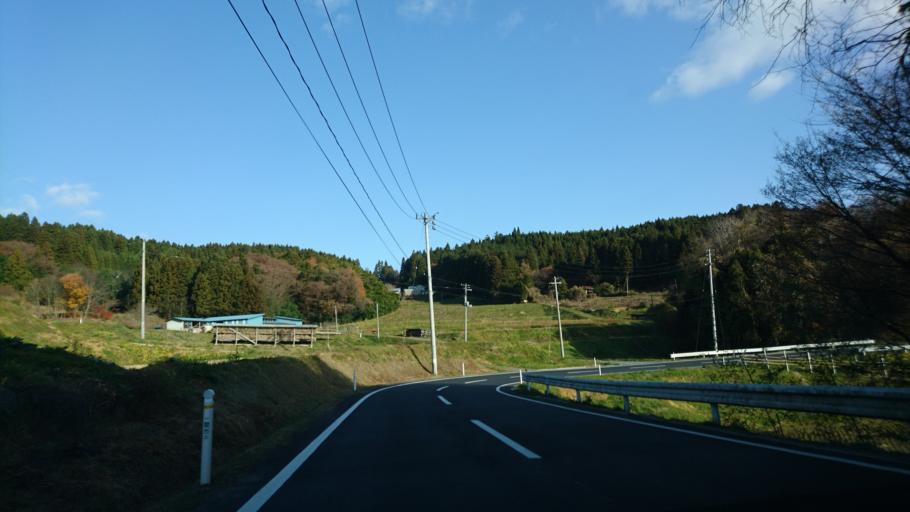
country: JP
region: Iwate
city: Ichinoseki
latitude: 38.8735
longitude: 141.3168
